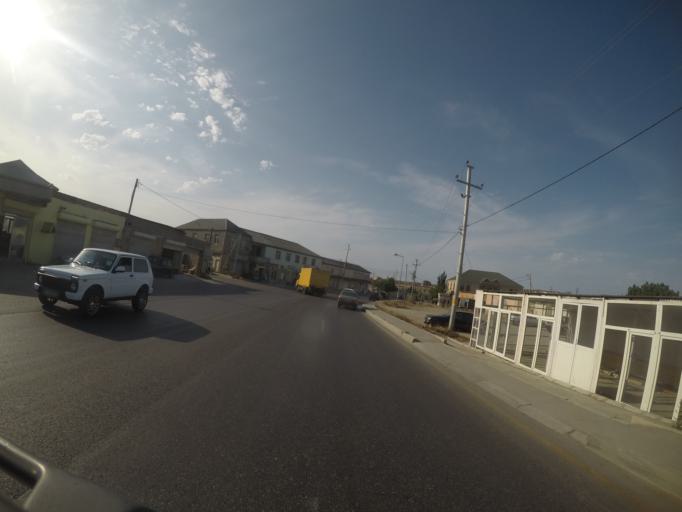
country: AZ
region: Baki
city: Binagadi
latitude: 40.4761
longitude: 49.8332
